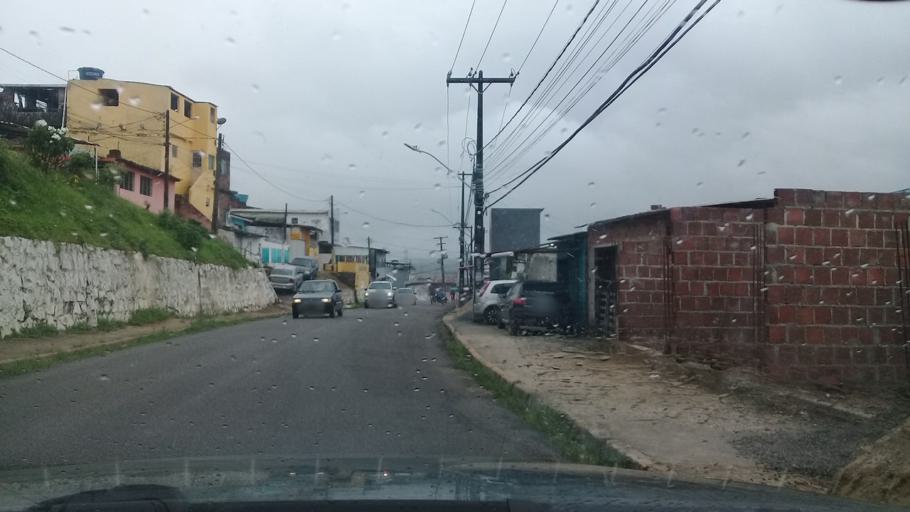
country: BR
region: Pernambuco
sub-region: Jaboatao Dos Guararapes
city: Jaboatao dos Guararapes
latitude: -8.0860
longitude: -34.9759
